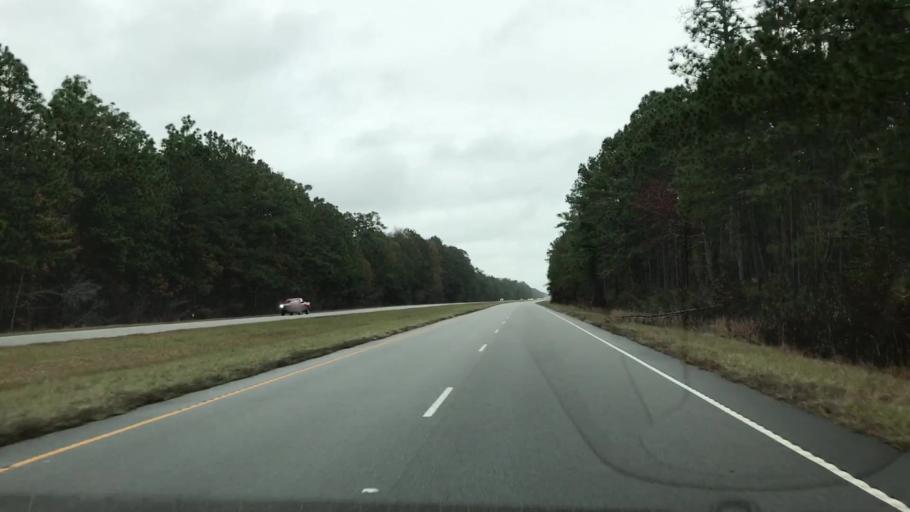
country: US
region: South Carolina
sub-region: Charleston County
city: Awendaw
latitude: 33.1318
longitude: -79.4456
